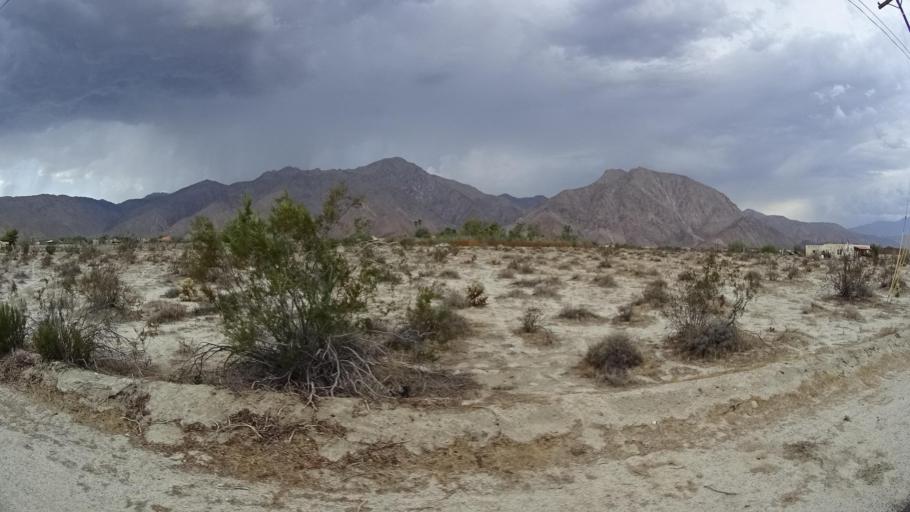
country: US
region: California
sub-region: San Diego County
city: Borrego Springs
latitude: 33.2612
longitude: -116.3859
